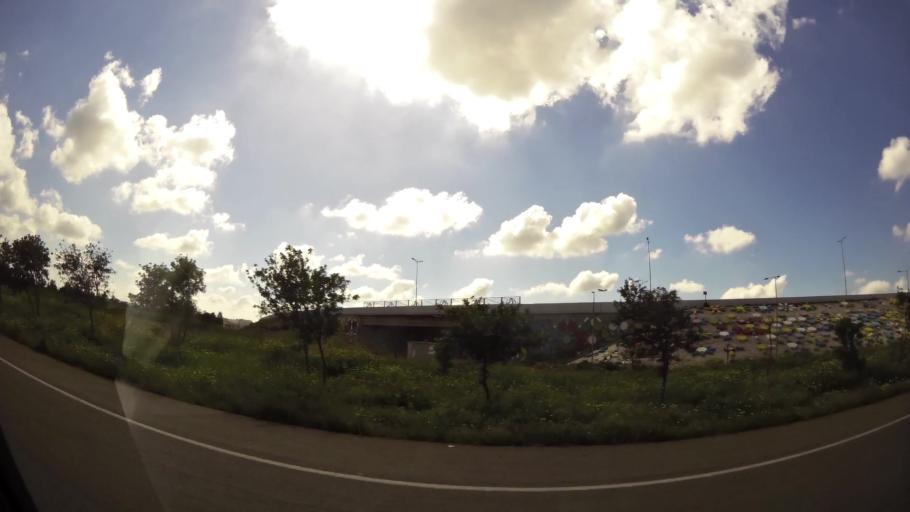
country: MA
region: Grand Casablanca
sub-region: Nouaceur
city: Bouskoura
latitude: 33.4324
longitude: -7.6280
